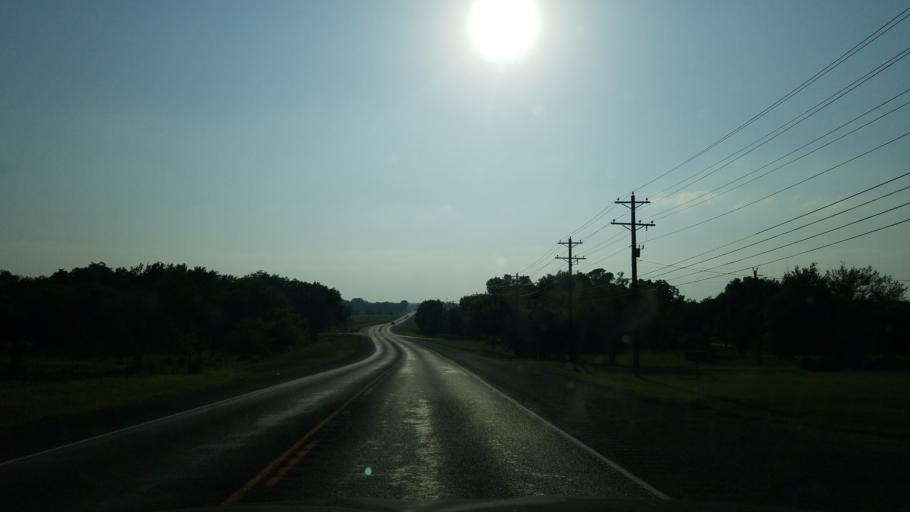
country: US
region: Texas
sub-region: Denton County
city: Aubrey
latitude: 33.3051
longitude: -97.0261
